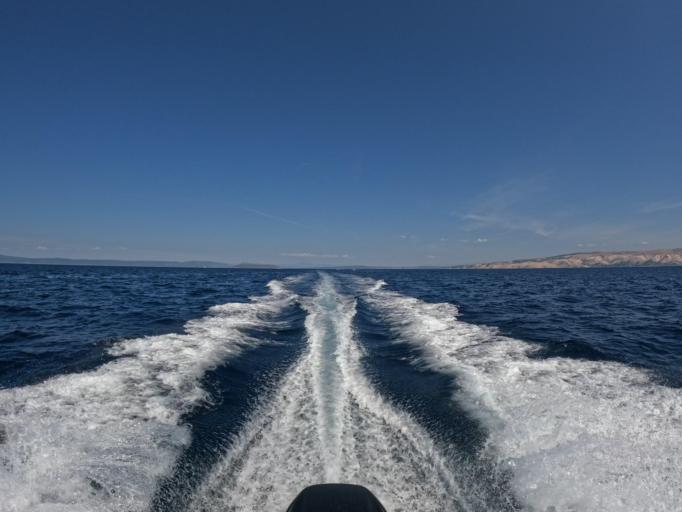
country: HR
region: Primorsko-Goranska
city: Lopar
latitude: 44.8917
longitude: 14.6439
